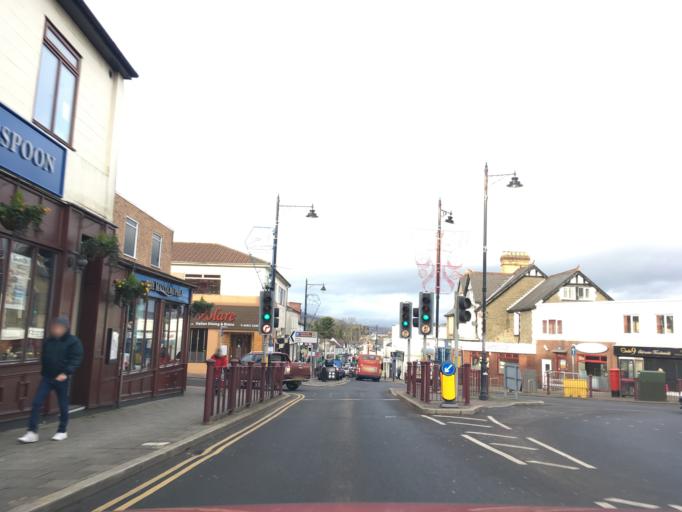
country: GB
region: Wales
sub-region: Caerphilly County Borough
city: Caerphilly
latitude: 51.5721
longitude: -3.2197
